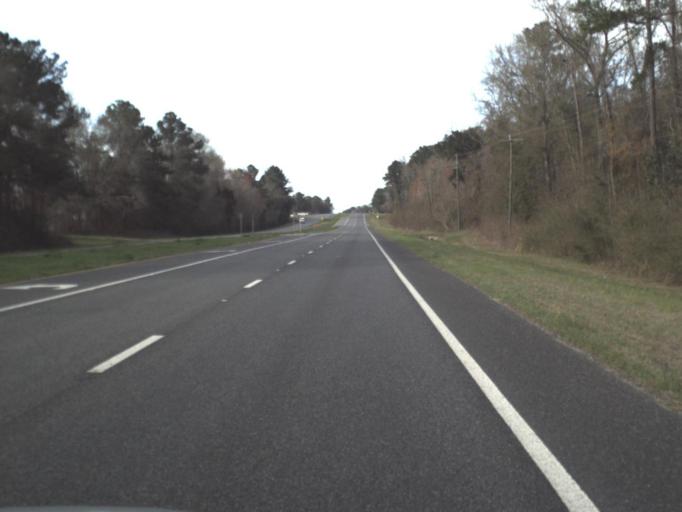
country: US
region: Florida
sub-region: Jefferson County
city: Monticello
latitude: 30.5760
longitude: -83.8699
